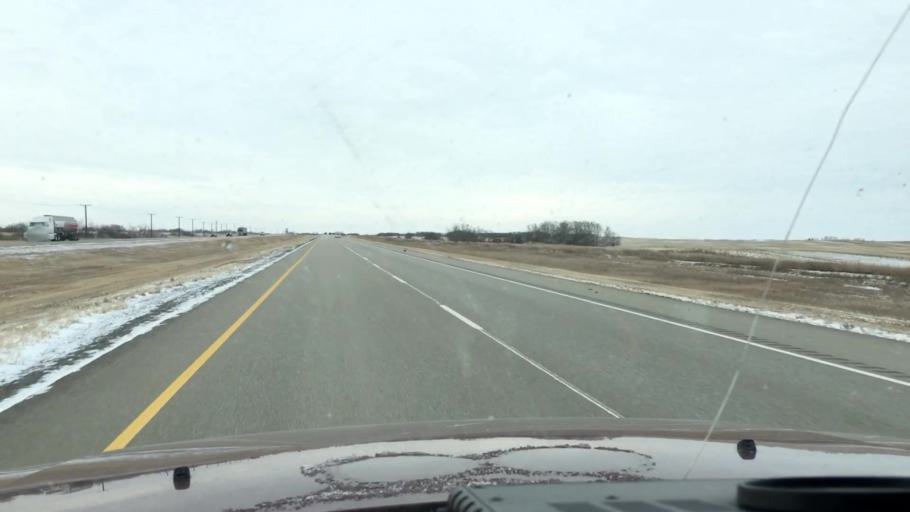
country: CA
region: Saskatchewan
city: Watrous
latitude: 51.3980
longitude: -106.1745
